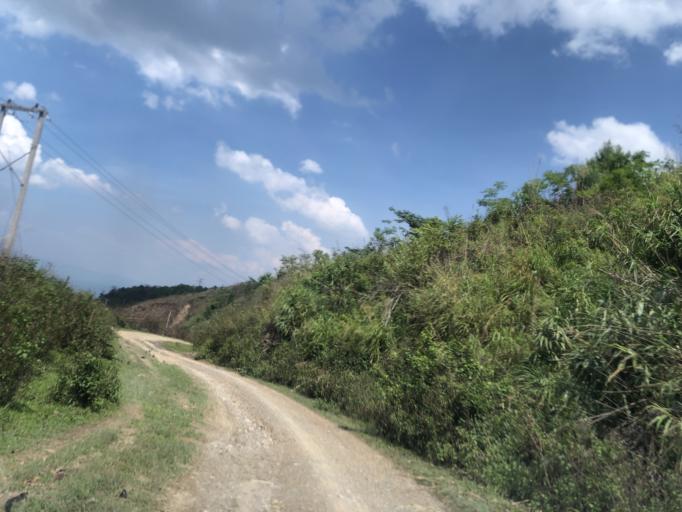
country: LA
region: Phongsali
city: Phongsali
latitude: 21.3966
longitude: 102.2165
